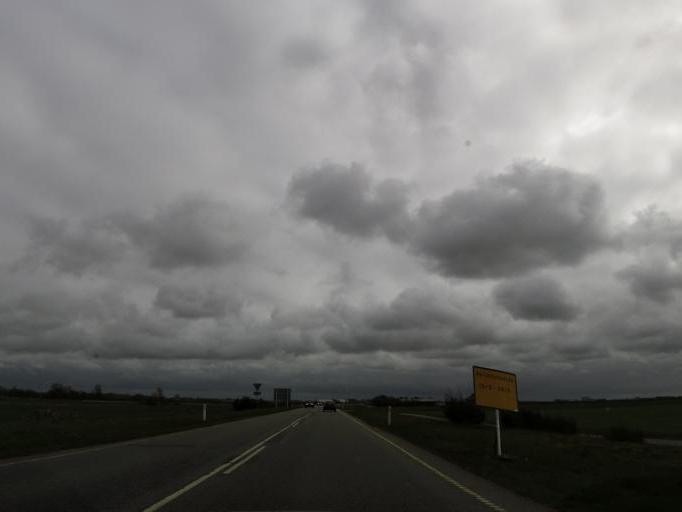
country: DK
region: South Denmark
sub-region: Tonder Kommune
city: Tonder
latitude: 54.9292
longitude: 8.8915
